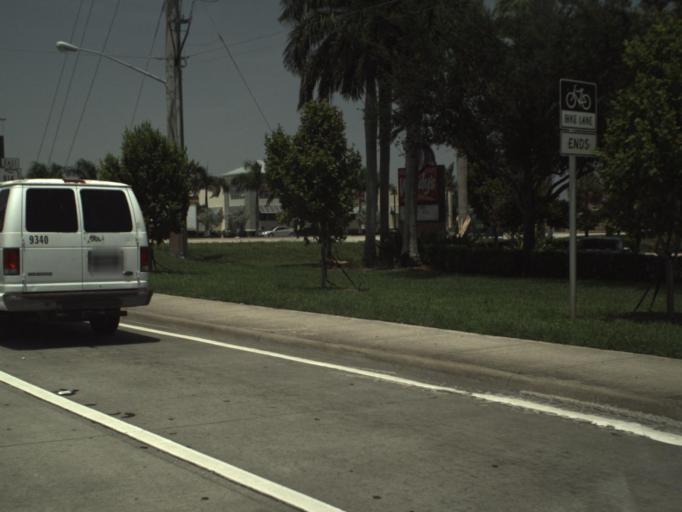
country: US
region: Florida
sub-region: Broward County
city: Coconut Creek
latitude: 26.2305
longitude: -80.1566
